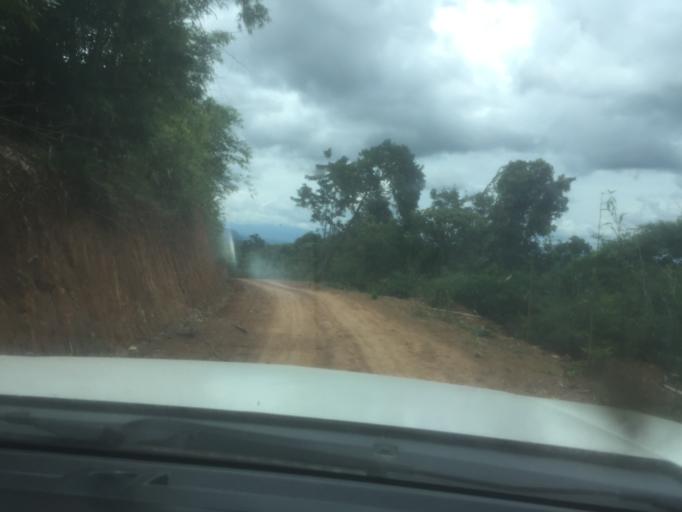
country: LA
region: Phongsali
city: Khoa
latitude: 20.9271
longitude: 102.5368
